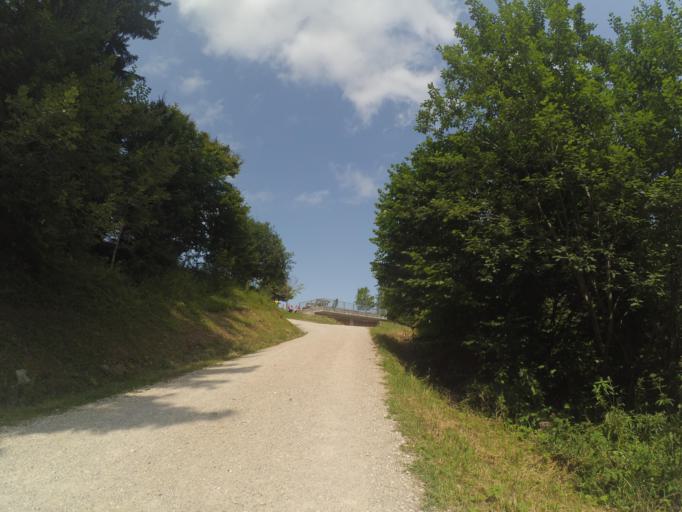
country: DE
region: Bavaria
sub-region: Swabia
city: Halblech
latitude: 47.6052
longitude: 10.8111
